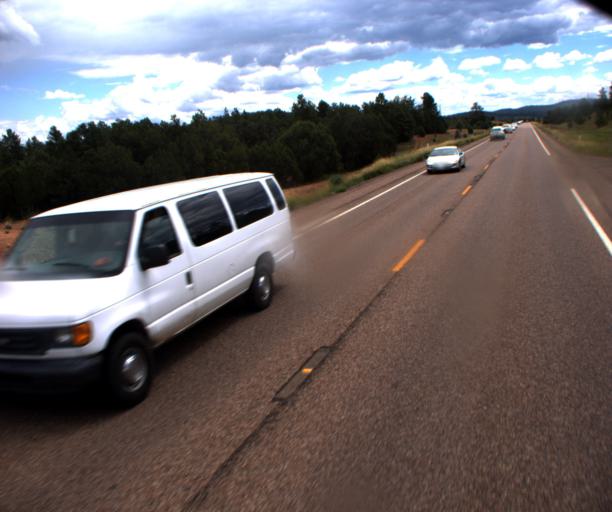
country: US
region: Arizona
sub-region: Navajo County
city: Linden
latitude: 34.3231
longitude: -110.2546
